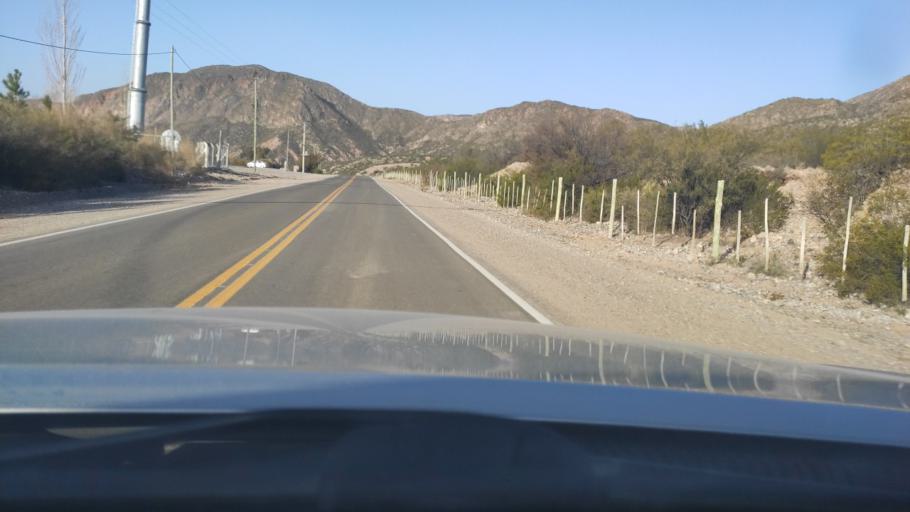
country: AR
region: San Juan
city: Villa Media Agua
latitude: -32.0029
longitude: -68.7625
